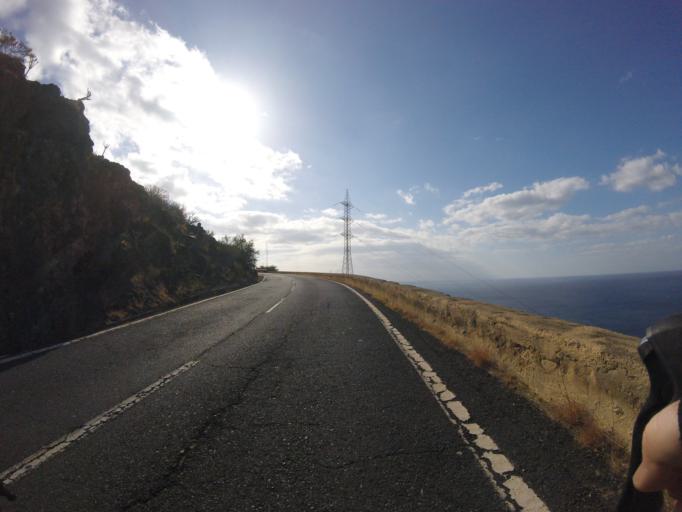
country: ES
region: Canary Islands
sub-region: Provincia de Santa Cruz de Tenerife
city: Candelaria
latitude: 28.3852
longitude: -16.3571
